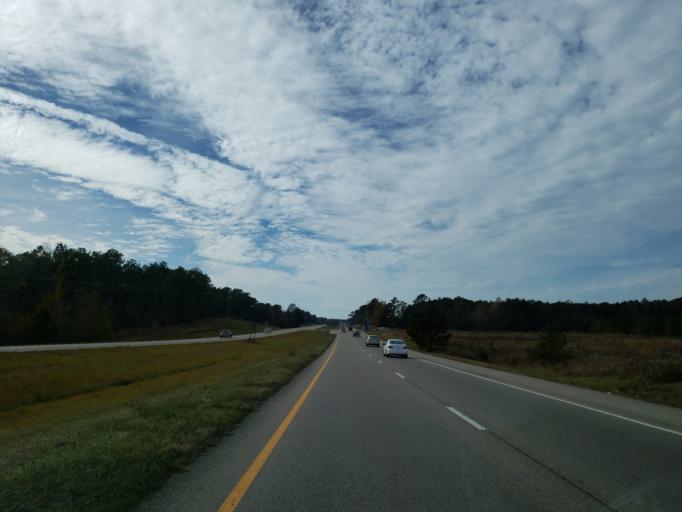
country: US
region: Mississippi
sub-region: Lamar County
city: West Hattiesburg
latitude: 31.3152
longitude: -89.4471
